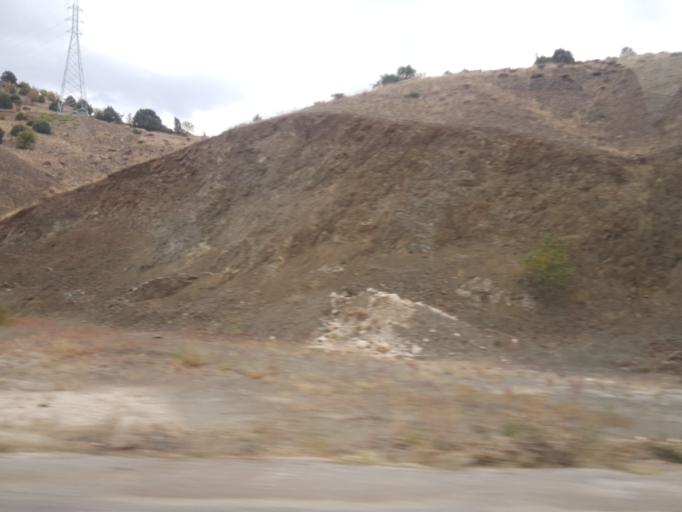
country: TR
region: Yozgat
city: Cekerek
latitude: 40.1985
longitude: 35.4534
